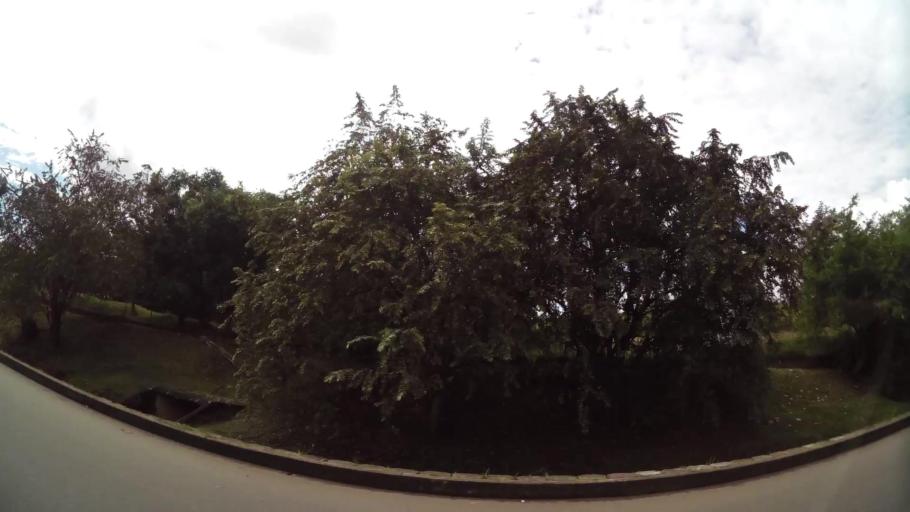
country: CO
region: Valle del Cauca
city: Cali
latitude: 3.3856
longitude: -76.5490
